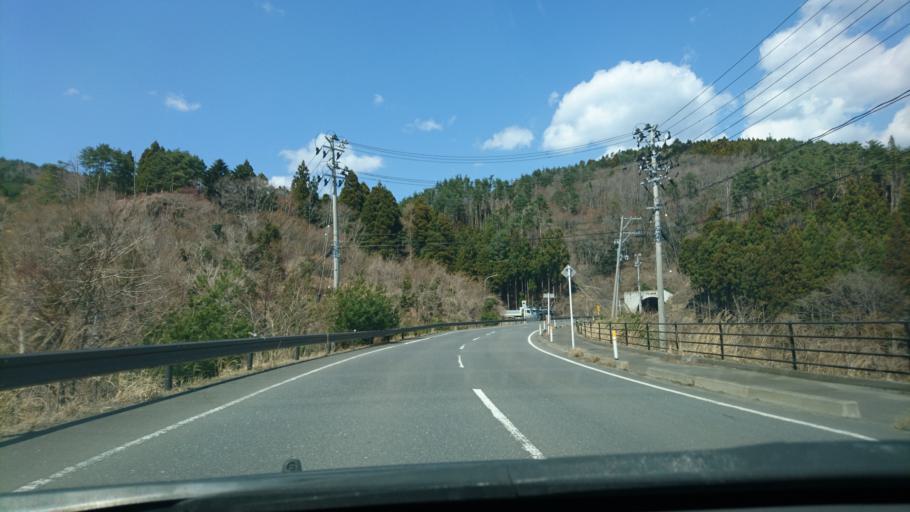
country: JP
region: Miyagi
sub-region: Oshika Gun
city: Onagawa Cho
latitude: 38.4881
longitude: 141.4876
